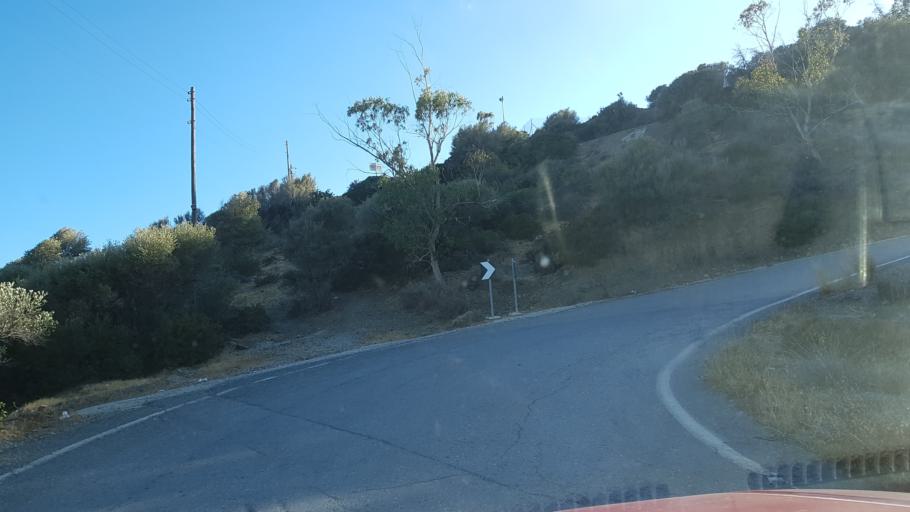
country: GR
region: Crete
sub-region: Nomos Irakleiou
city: Moires
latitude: 34.9340
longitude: 24.8047
